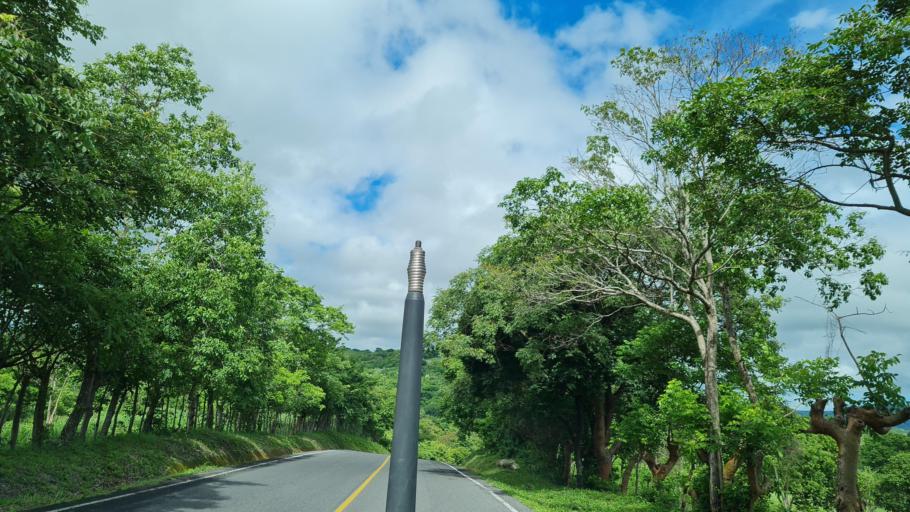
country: NI
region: Boaco
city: San Jose de los Remates
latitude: 12.6126
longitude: -85.8835
